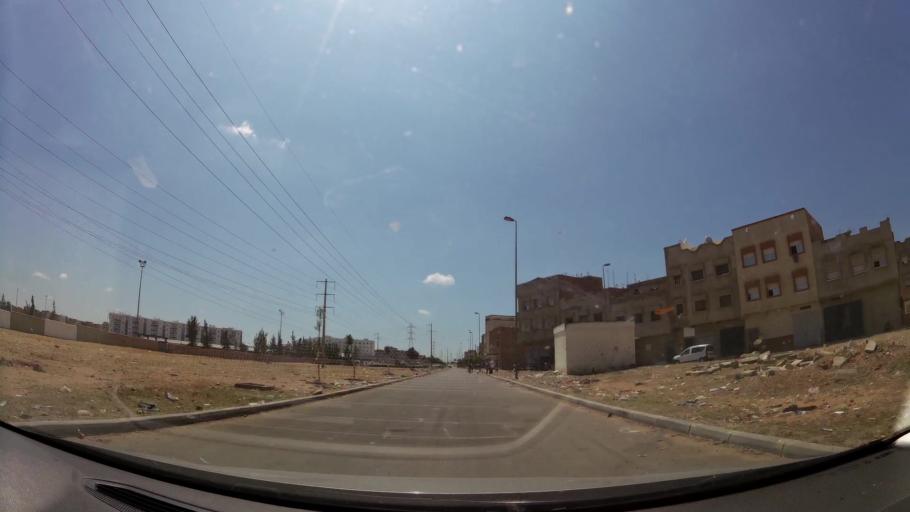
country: MA
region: Gharb-Chrarda-Beni Hssen
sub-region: Kenitra Province
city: Kenitra
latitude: 34.2379
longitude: -6.5402
